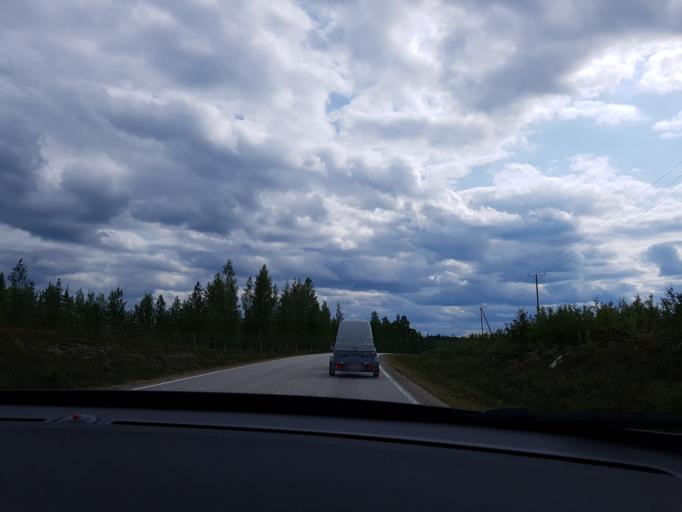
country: FI
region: Kainuu
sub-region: Kehys-Kainuu
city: Kuhmo
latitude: 64.2529
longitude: 29.8105
